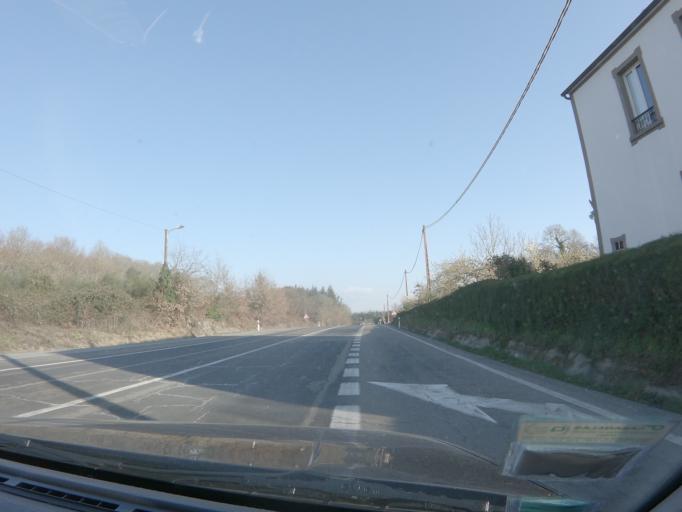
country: ES
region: Galicia
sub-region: Provincia de Lugo
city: Corgo
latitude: 42.9546
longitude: -7.4647
